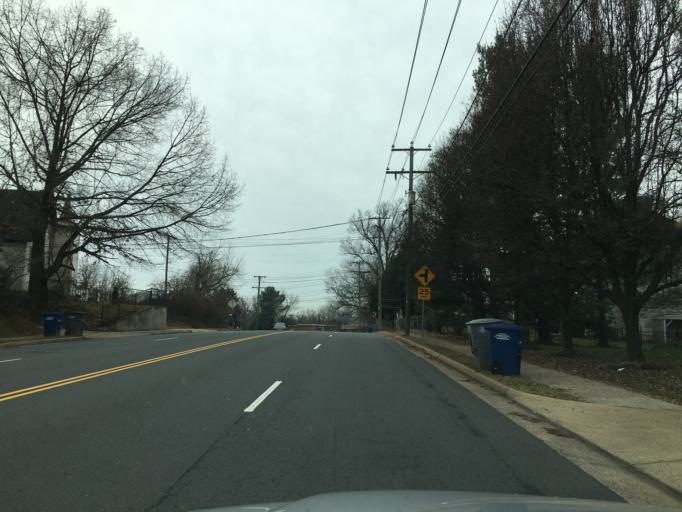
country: US
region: Virginia
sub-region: City of Falls Church
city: Falls Church
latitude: 38.8773
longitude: -77.1738
